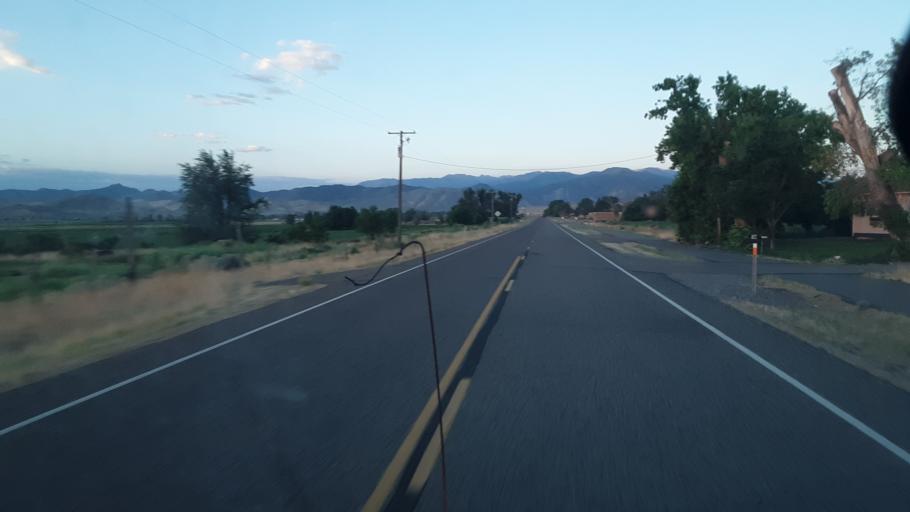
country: US
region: Utah
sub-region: Sevier County
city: Monroe
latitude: 38.6488
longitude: -112.2103
